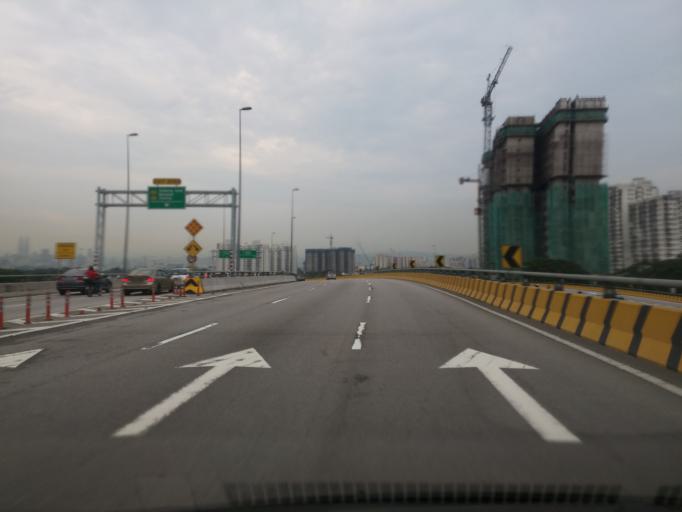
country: MY
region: Kuala Lumpur
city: Kuala Lumpur
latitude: 3.0893
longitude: 101.6952
